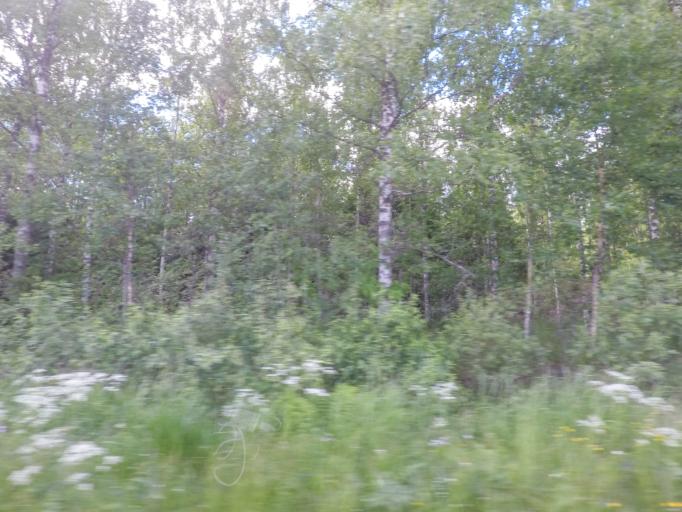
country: FI
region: Central Finland
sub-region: Jyvaeskylae
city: Hankasalmi
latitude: 62.4162
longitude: 26.6406
